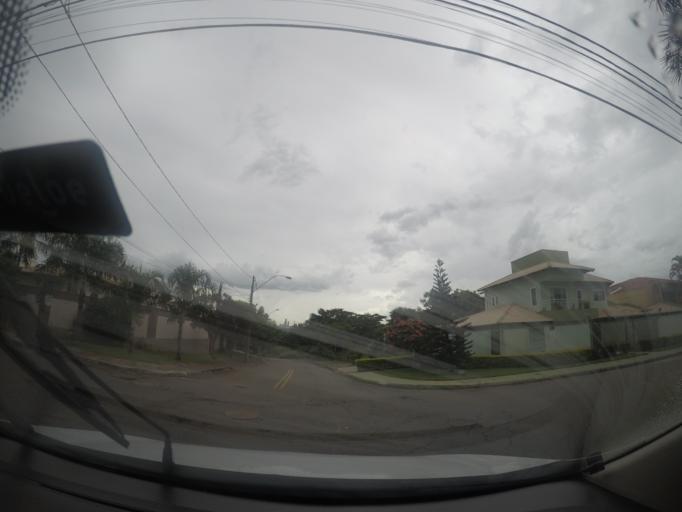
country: BR
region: Goias
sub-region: Goiania
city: Goiania
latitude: -16.6431
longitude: -49.2328
